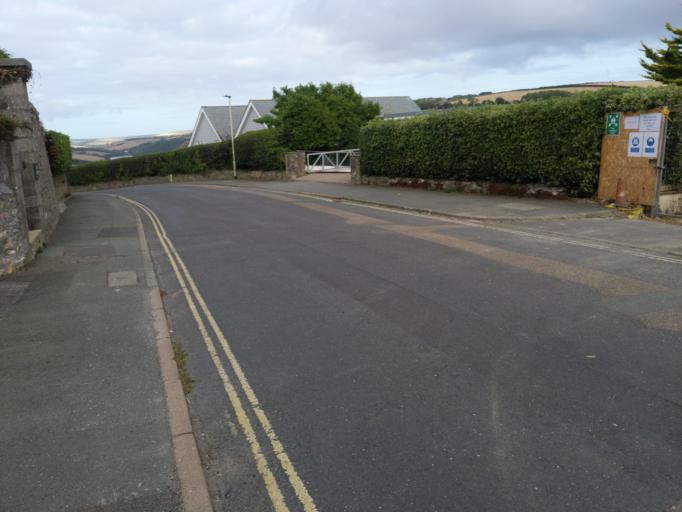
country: GB
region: England
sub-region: Devon
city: Salcombe
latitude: 50.2342
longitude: -3.7724
